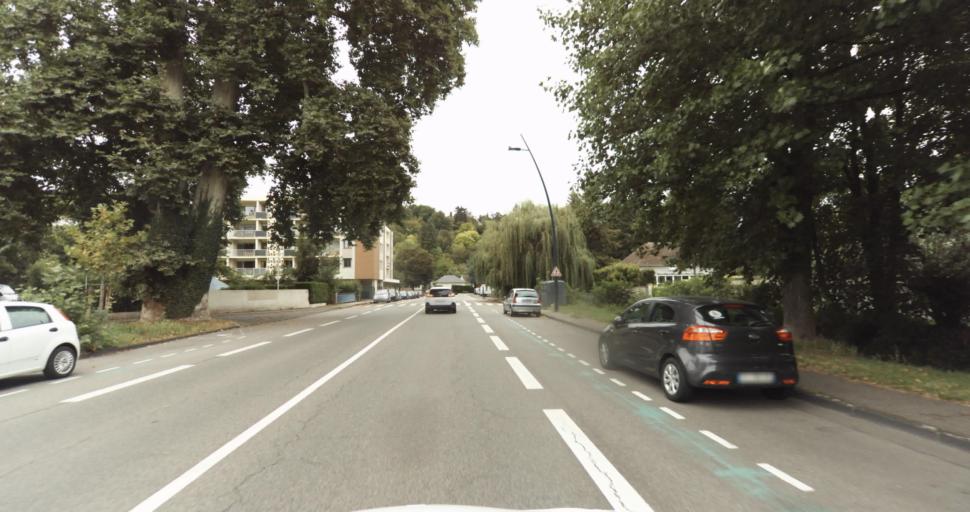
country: FR
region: Haute-Normandie
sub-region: Departement de l'Eure
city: Evreux
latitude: 49.0250
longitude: 1.1386
